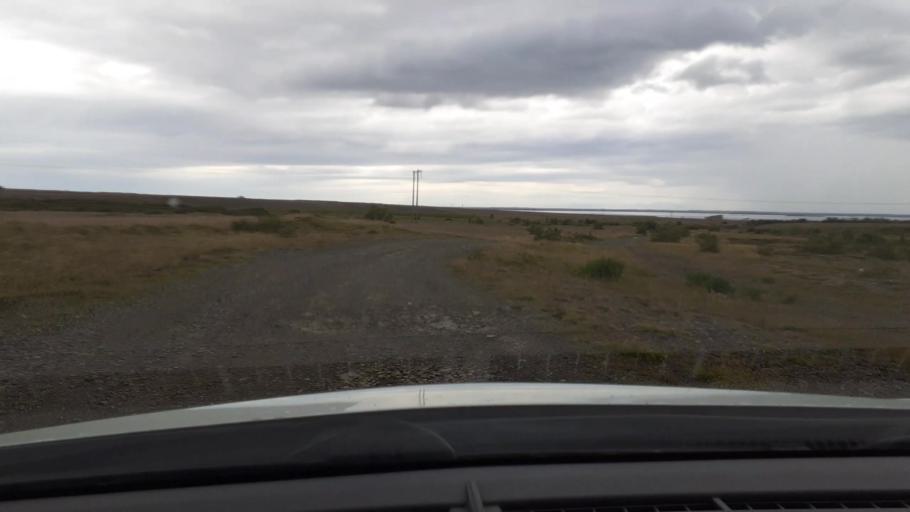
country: IS
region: West
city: Borgarnes
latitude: 64.4610
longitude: -21.9547
